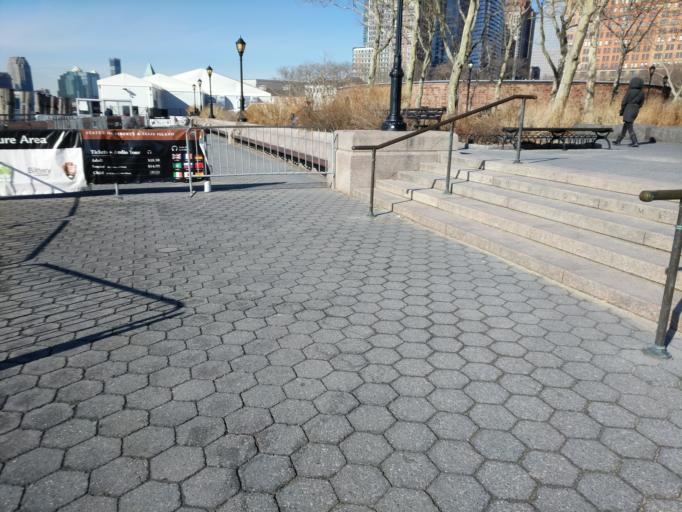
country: US
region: New York
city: New York City
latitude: 40.7025
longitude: -74.0167
